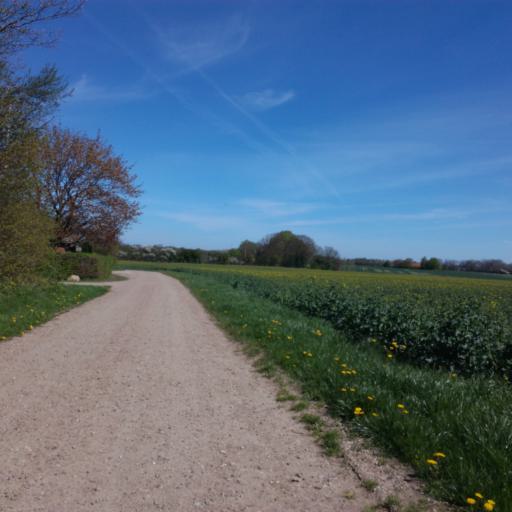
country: DK
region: South Denmark
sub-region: Vejle Kommune
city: Borkop
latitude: 55.6147
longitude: 9.6821
